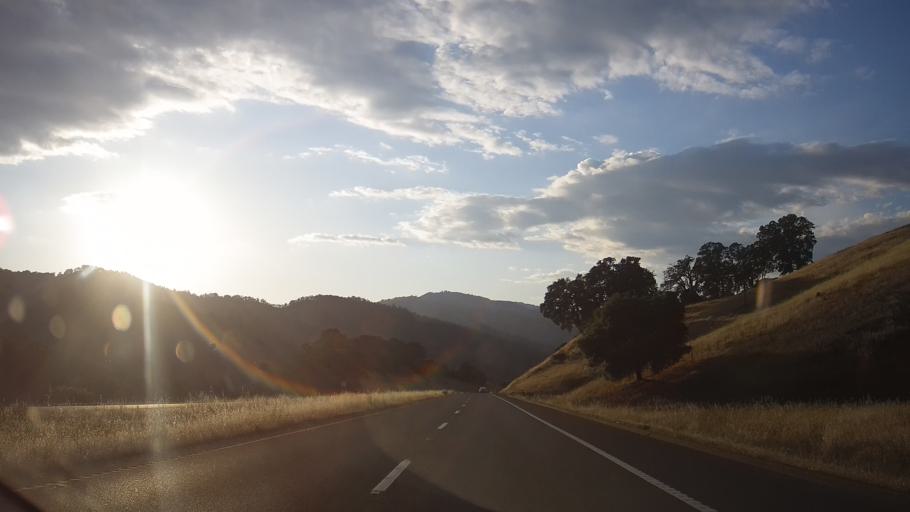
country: US
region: California
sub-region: Mendocino County
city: Talmage
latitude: 39.0754
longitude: -123.1756
